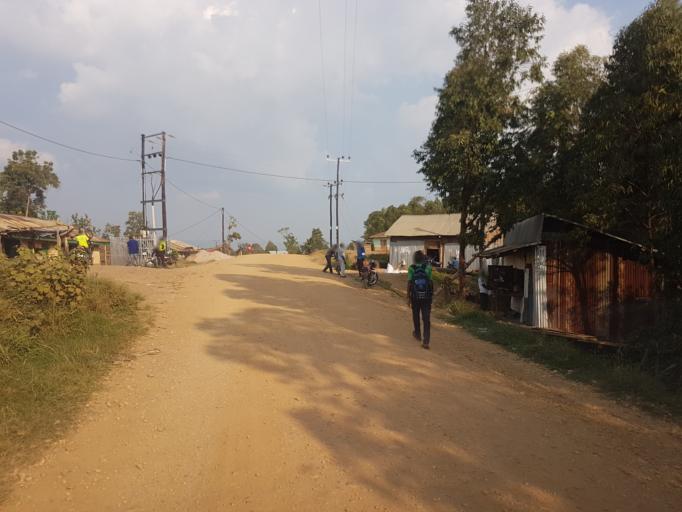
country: UG
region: Western Region
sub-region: Rukungiri District
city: Rukungiri
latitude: -0.6456
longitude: 29.8425
